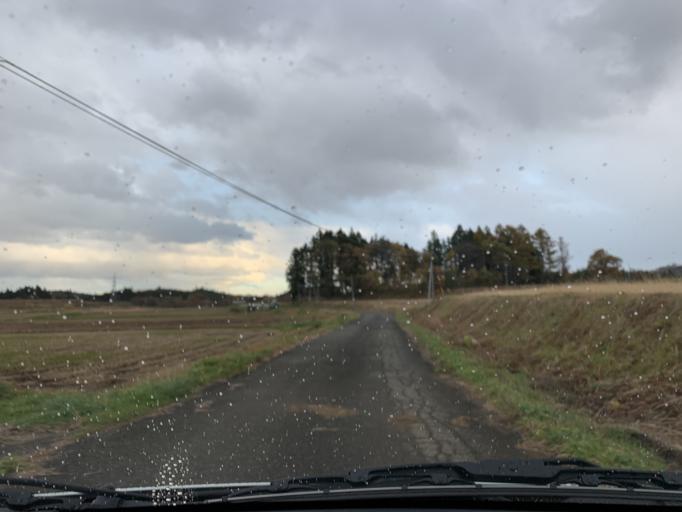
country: JP
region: Iwate
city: Mizusawa
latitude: 39.0876
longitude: 141.0005
